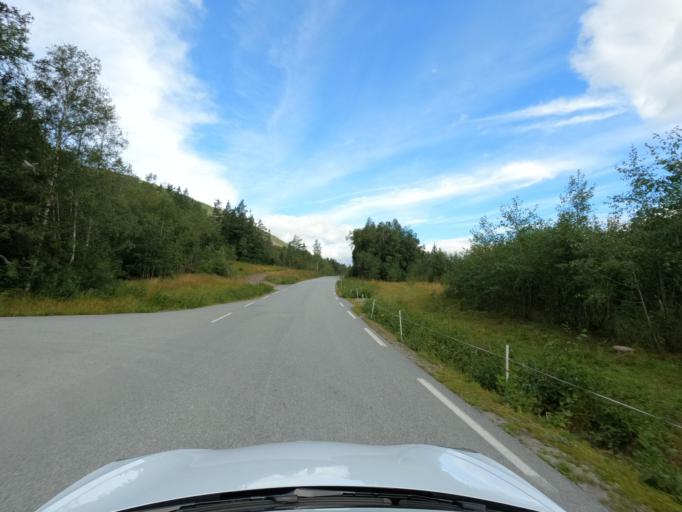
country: NO
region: Telemark
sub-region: Tinn
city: Rjukan
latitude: 60.0184
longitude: 8.7434
